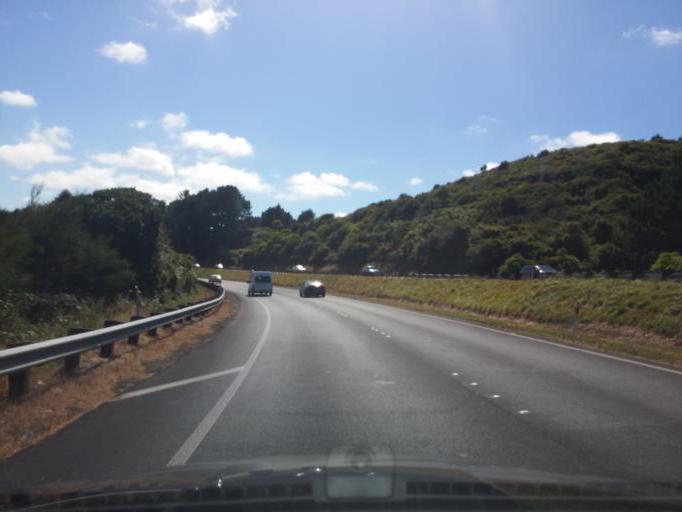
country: NZ
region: Wellington
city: Petone
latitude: -41.1939
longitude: 174.8294
